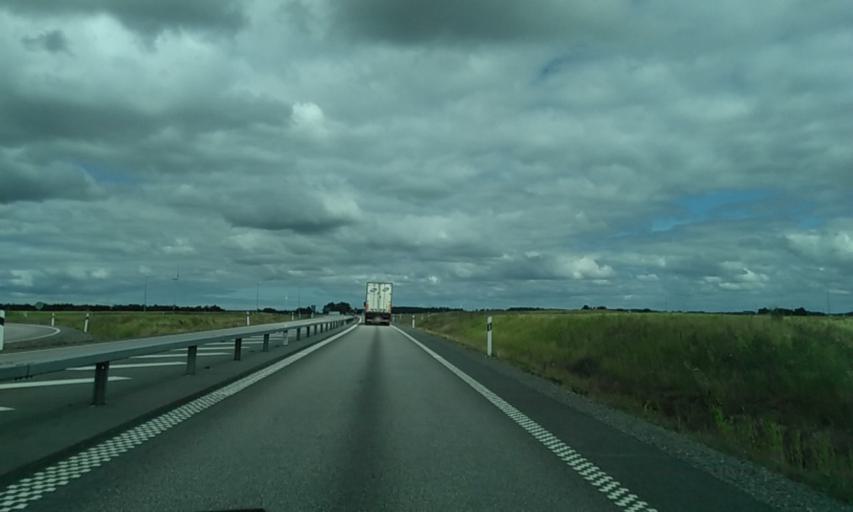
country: SE
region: Vaestra Goetaland
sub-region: Vara Kommun
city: Kvanum
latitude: 58.3272
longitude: 13.1339
